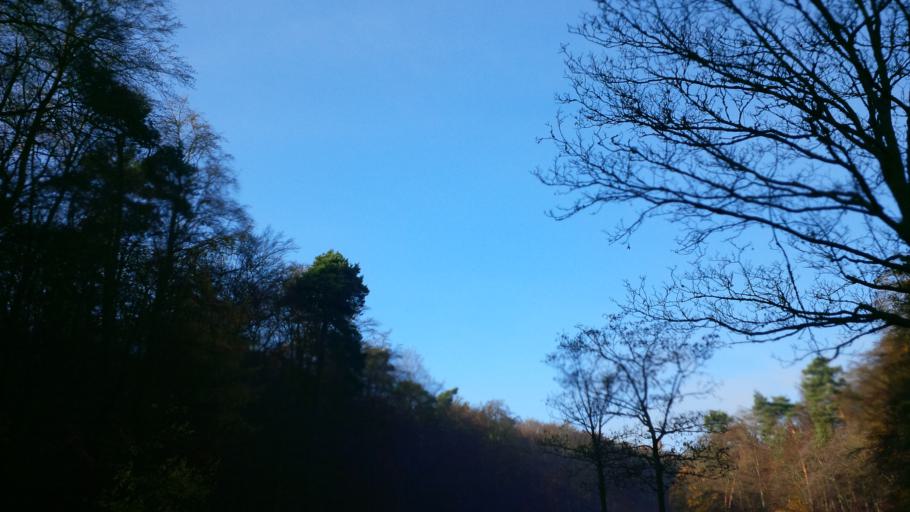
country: DE
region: Hesse
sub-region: Regierungsbezirk Darmstadt
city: Neu-Anspach
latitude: 50.2847
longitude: 8.4904
